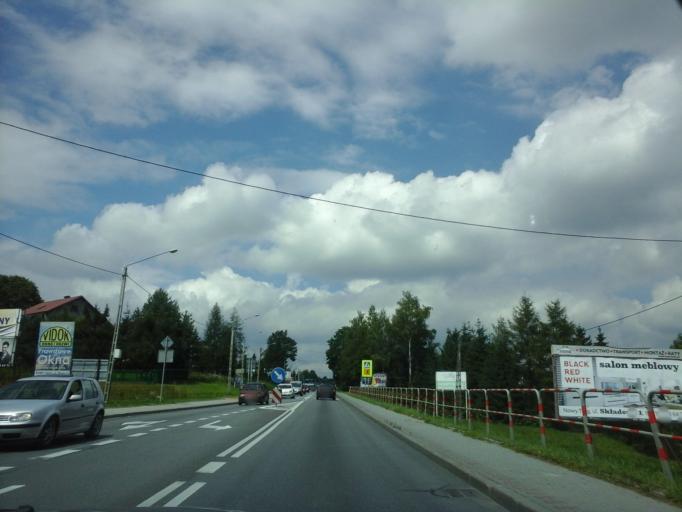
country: PL
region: Lesser Poland Voivodeship
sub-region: Powiat nowotarski
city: Nowy Targ
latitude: 49.4919
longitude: 20.0135
